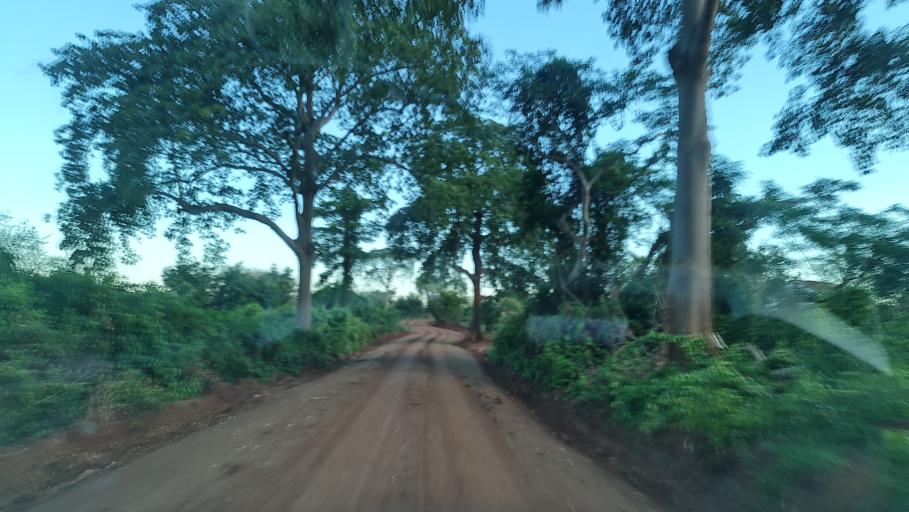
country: MZ
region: Nampula
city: Ilha de Mocambique
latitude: -14.9809
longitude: 40.0939
